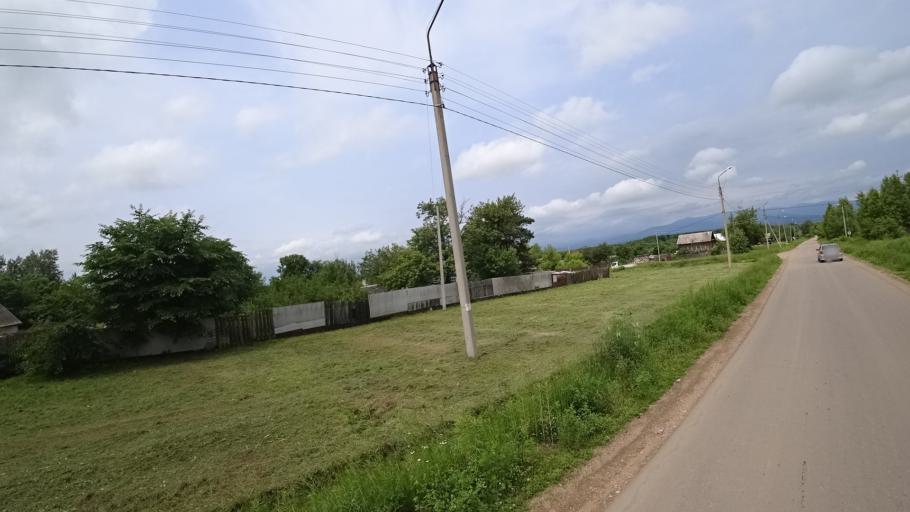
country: RU
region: Primorskiy
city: Novosysoyevka
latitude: 44.2347
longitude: 133.3593
